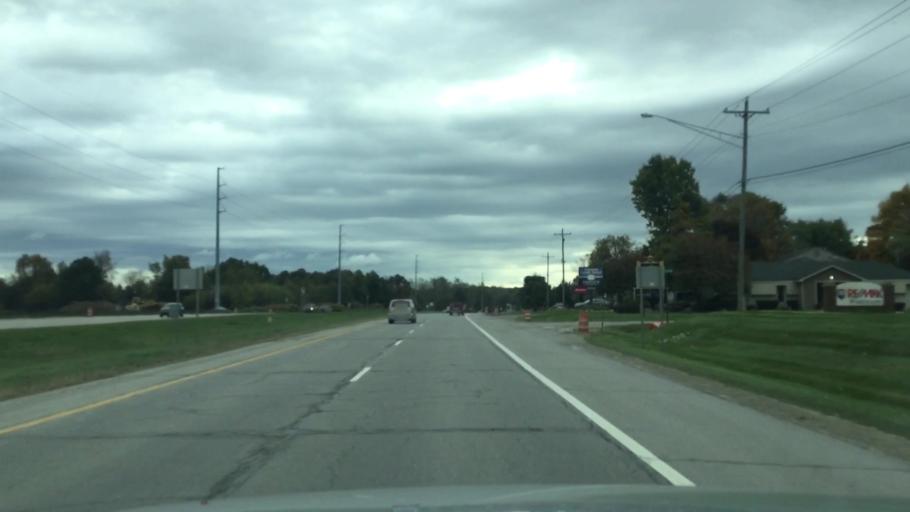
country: US
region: Michigan
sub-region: Livingston County
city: Brighton
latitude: 42.6359
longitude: -83.7295
